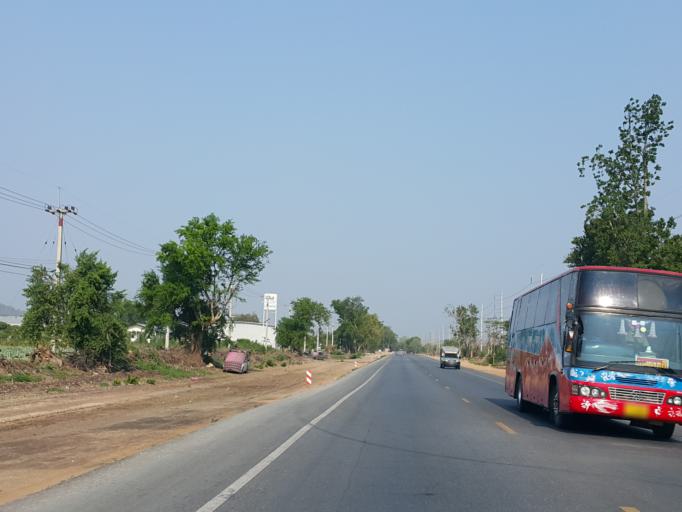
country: TH
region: Kanchanaburi
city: Sai Yok
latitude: 14.0890
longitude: 99.3226
